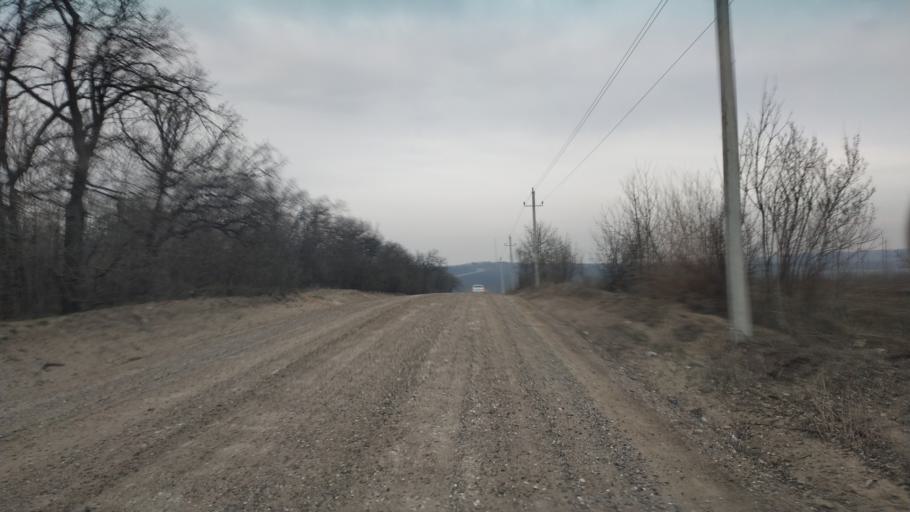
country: MD
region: Chisinau
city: Singera
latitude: 46.8527
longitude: 29.0132
